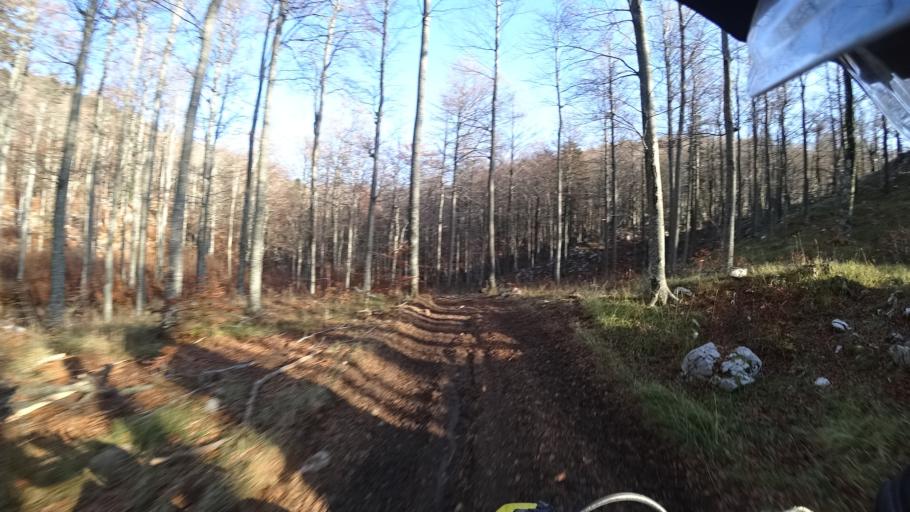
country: HR
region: Primorsko-Goranska
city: Klana
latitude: 45.4805
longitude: 14.4453
